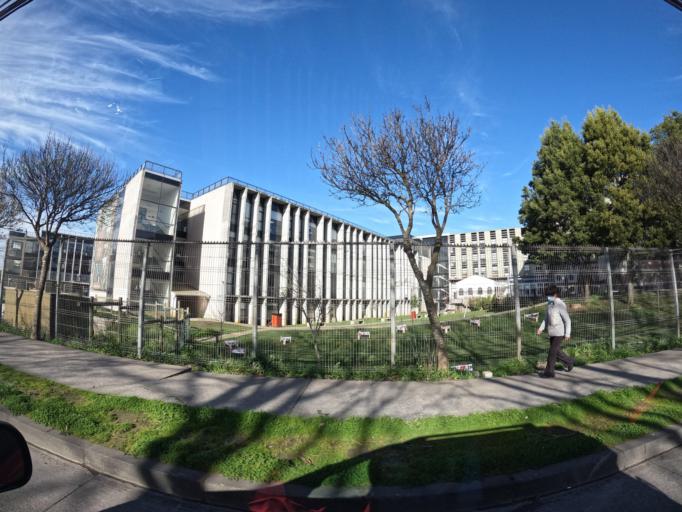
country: CL
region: Biobio
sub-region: Provincia de Concepcion
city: Concepcion
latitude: -36.7795
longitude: -73.0766
